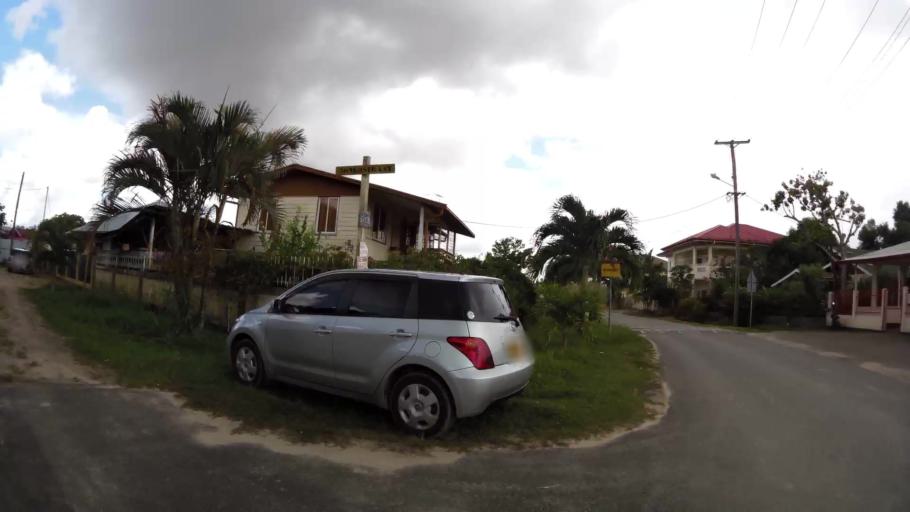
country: SR
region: Paramaribo
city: Paramaribo
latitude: 5.8375
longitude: -55.2000
